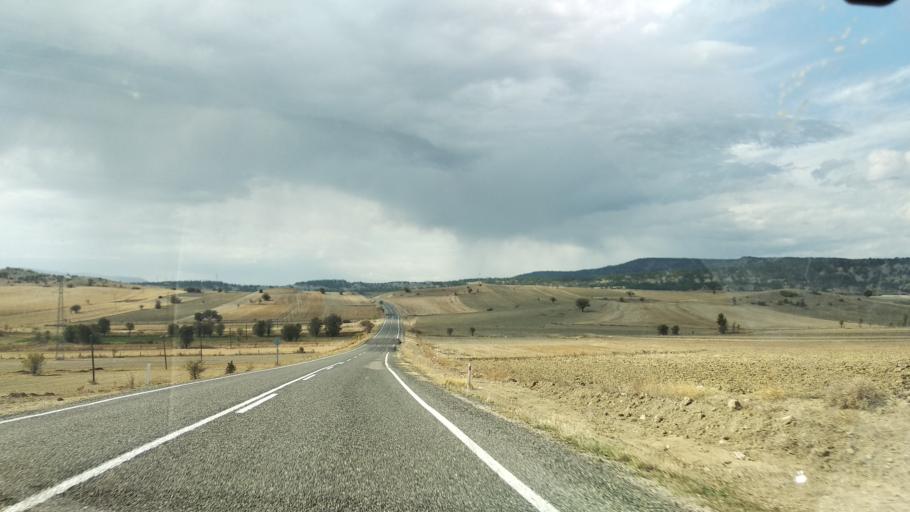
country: TR
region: Bolu
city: Seben
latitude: 40.3708
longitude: 31.5084
